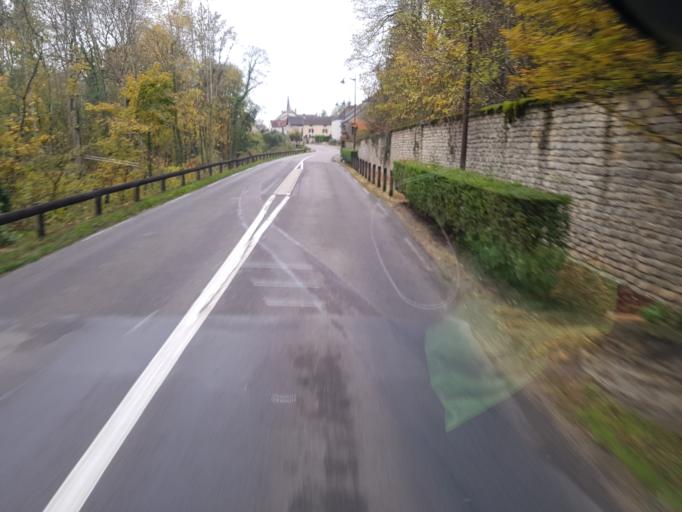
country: FR
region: Bourgogne
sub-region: Departement de la Cote-d'Or
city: Is-sur-Tille
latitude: 47.5406
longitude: 4.9721
